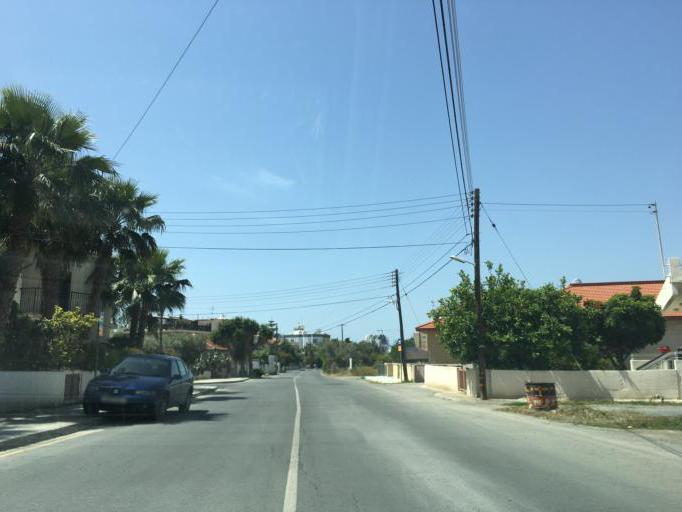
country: CY
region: Limassol
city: Mouttagiaka
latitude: 34.6991
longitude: 33.0819
